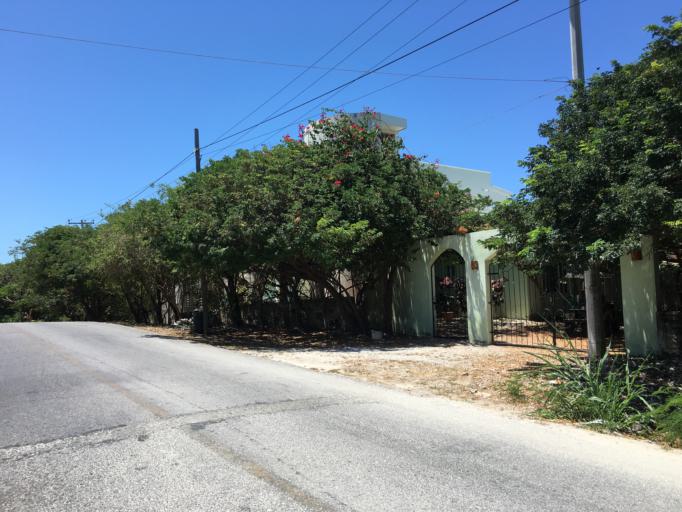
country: MX
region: Quintana Roo
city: Isla Mujeres
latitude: 21.2080
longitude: -86.7187
